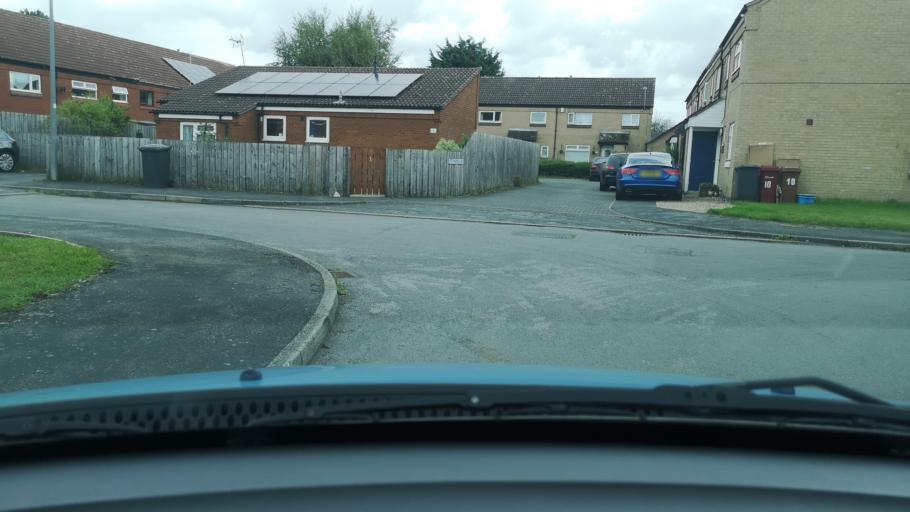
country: GB
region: England
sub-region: North Lincolnshire
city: Scunthorpe
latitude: 53.5867
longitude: -0.6898
